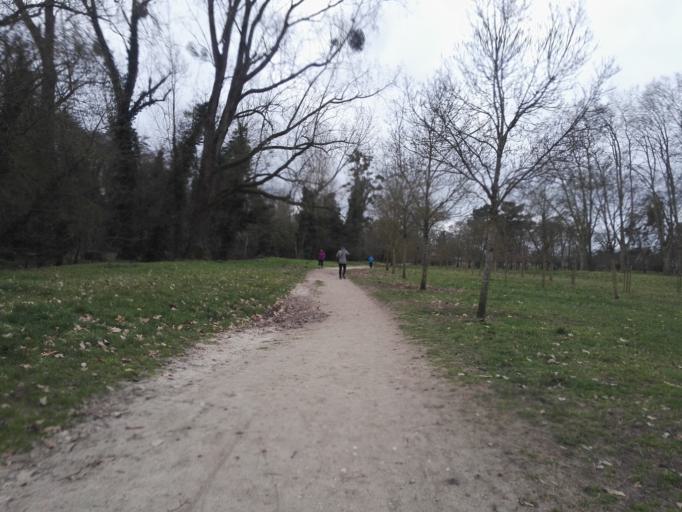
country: FR
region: Aquitaine
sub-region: Departement de la Gironde
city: Begles
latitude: 44.7934
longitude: -0.5576
